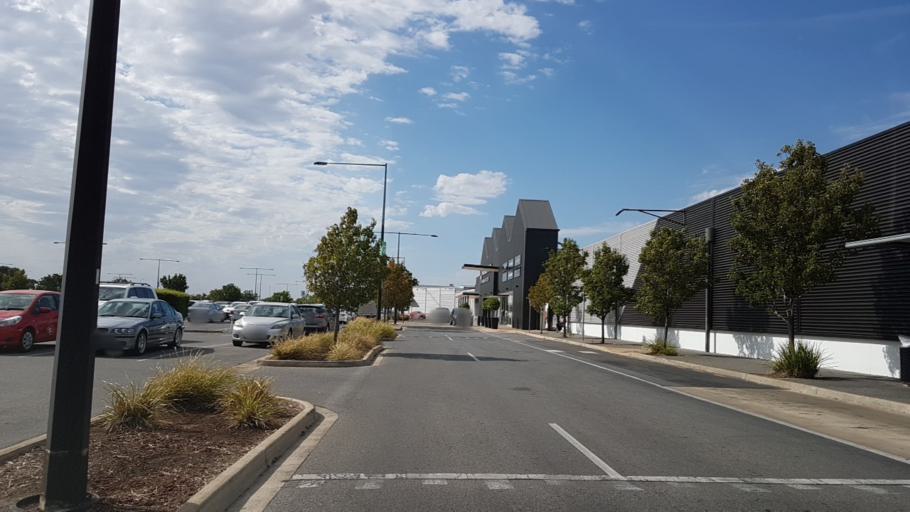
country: AU
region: South Australia
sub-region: City of West Torrens
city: Plympton
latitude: -34.9471
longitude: 138.5200
